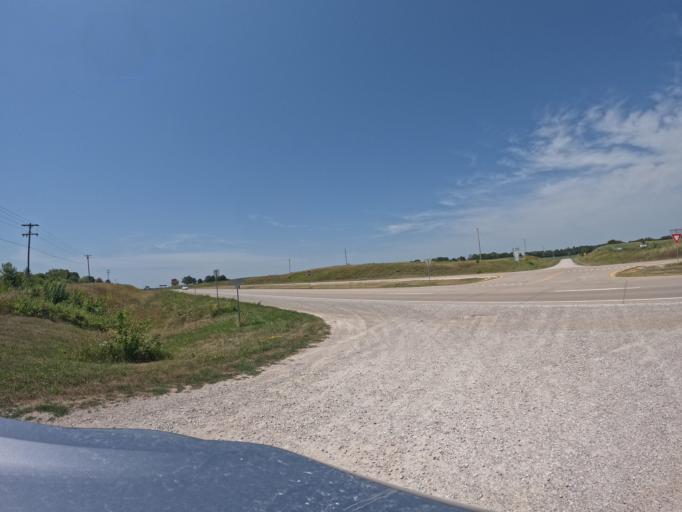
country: US
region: Iowa
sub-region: Henry County
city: Mount Pleasant
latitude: 40.9743
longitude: -91.6603
